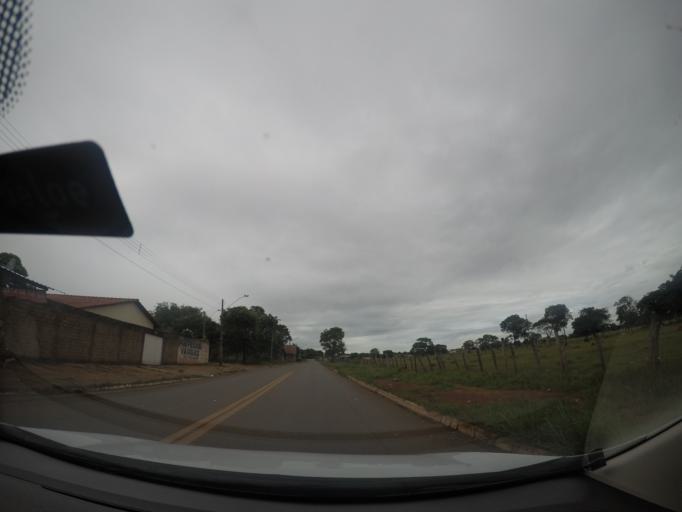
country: BR
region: Goias
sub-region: Goiania
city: Goiania
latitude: -16.6129
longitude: -49.3499
